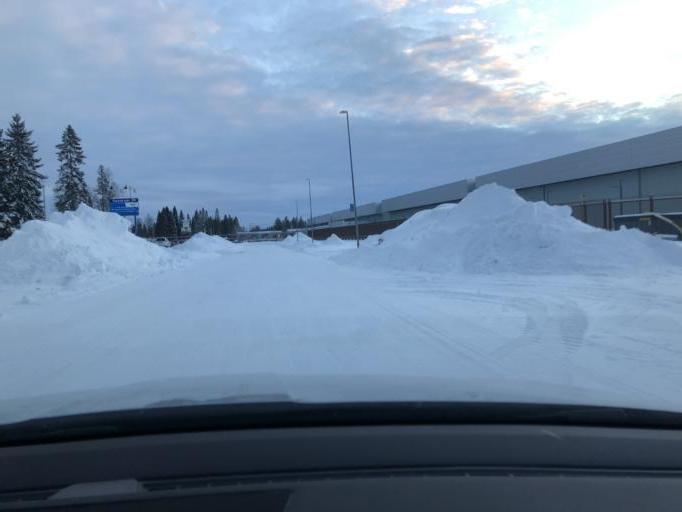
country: SE
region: Norrbotten
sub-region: Lulea Kommun
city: Bergnaset
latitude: 65.6185
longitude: 22.1155
